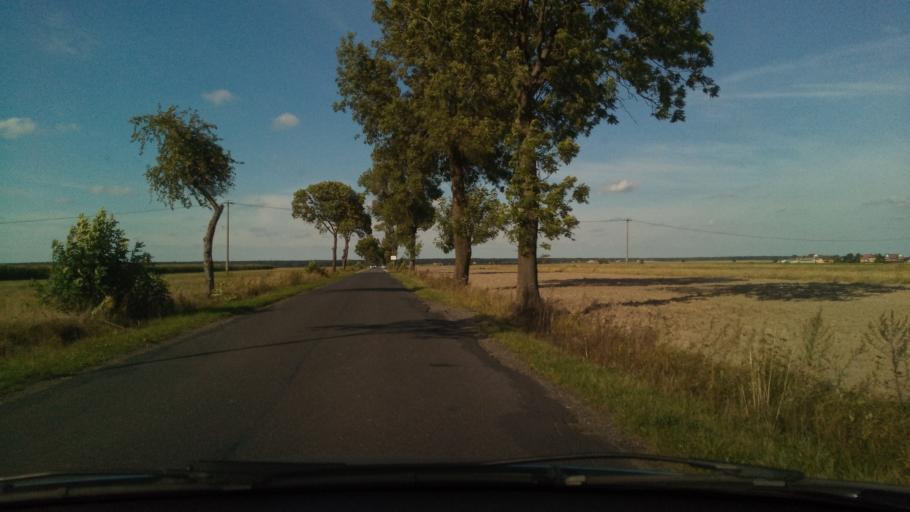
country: PL
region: Lodz Voivodeship
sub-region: Powiat piotrkowski
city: Sulejow
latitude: 51.3813
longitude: 19.8179
